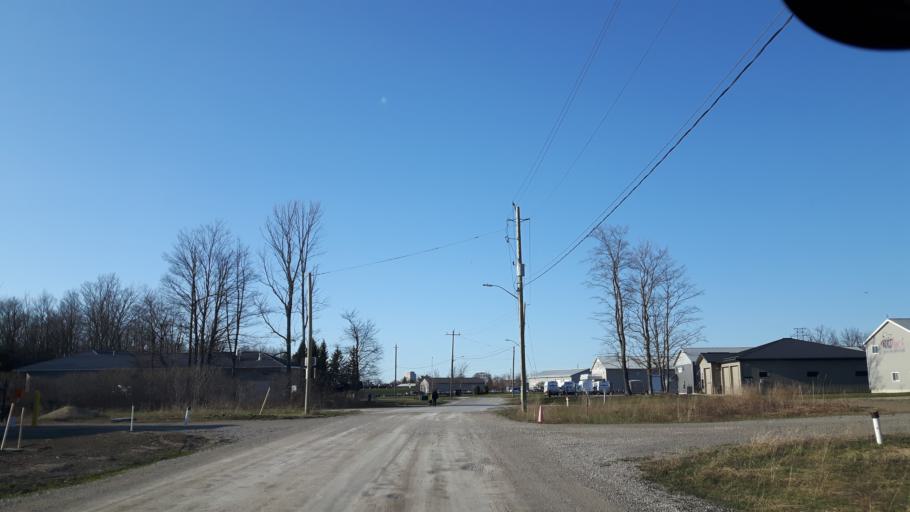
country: CA
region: Ontario
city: Goderich
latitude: 43.7273
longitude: -81.6936
